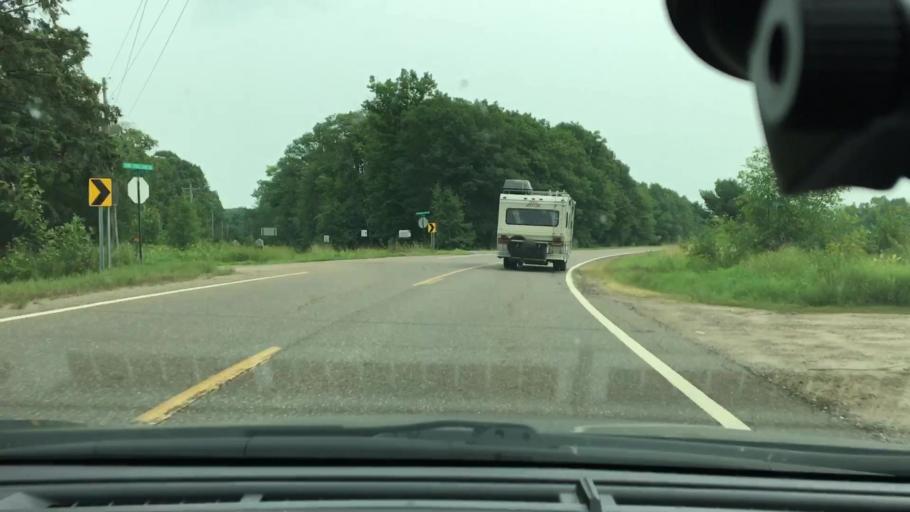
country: US
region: Minnesota
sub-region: Aitkin County
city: Aitkin
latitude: 46.4026
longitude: -93.7622
